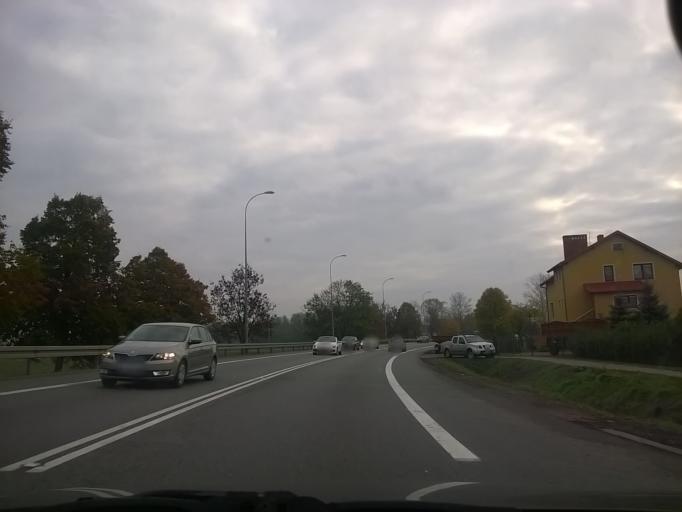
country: PL
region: Pomeranian Voivodeship
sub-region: Powiat nowodworski
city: Nowy Dwor Gdanski
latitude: 54.1870
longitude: 19.2109
